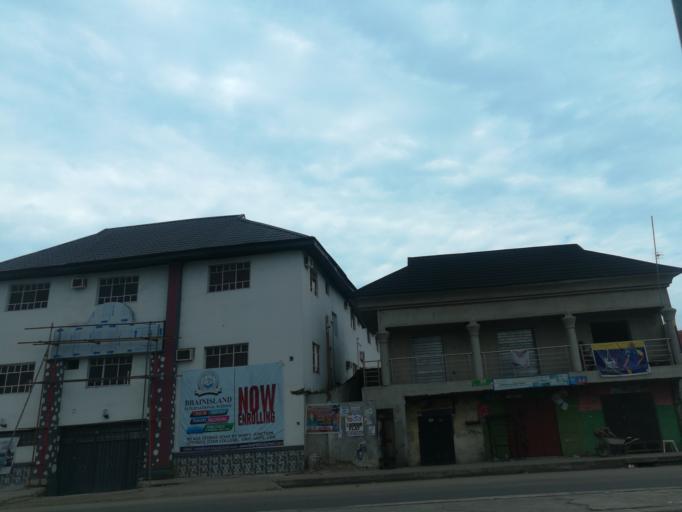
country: NG
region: Rivers
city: Port Harcourt
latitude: 4.8313
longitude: 6.9762
